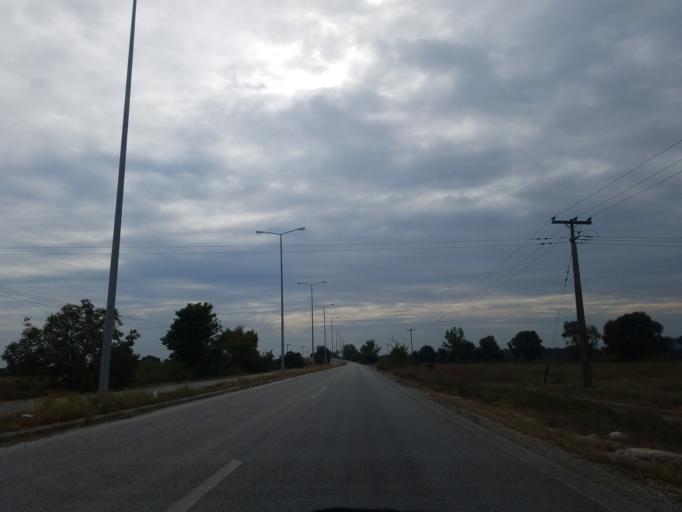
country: GR
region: Thessaly
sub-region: Trikala
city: Pyrgetos
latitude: 39.5246
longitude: 21.7503
